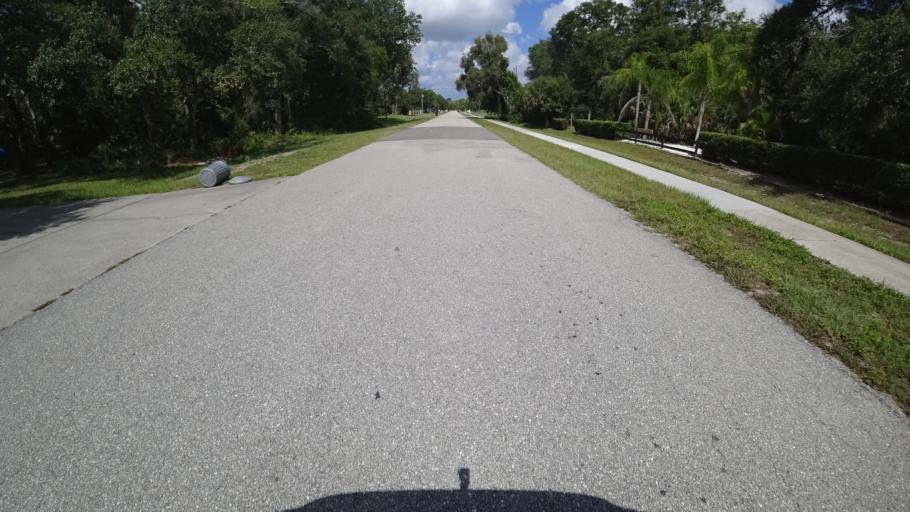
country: US
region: Florida
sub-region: Manatee County
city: Samoset
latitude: 27.4656
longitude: -82.4846
